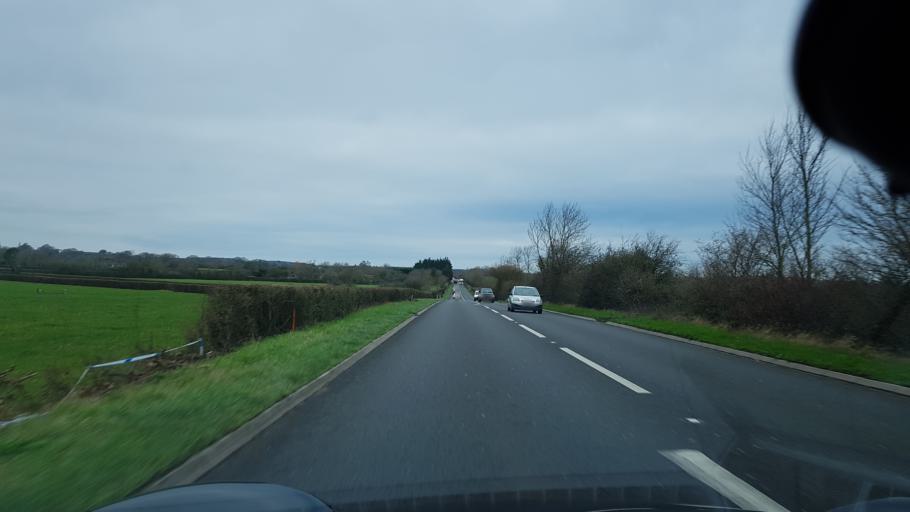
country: GB
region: England
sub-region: Somerset
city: Ilminster
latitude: 50.9594
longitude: -2.9843
